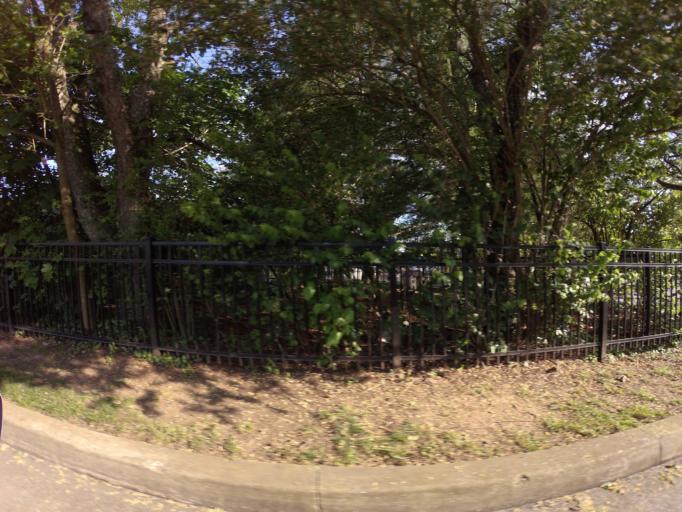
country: US
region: Maryland
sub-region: Baltimore County
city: Mays Chapel
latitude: 39.4260
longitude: -76.6763
